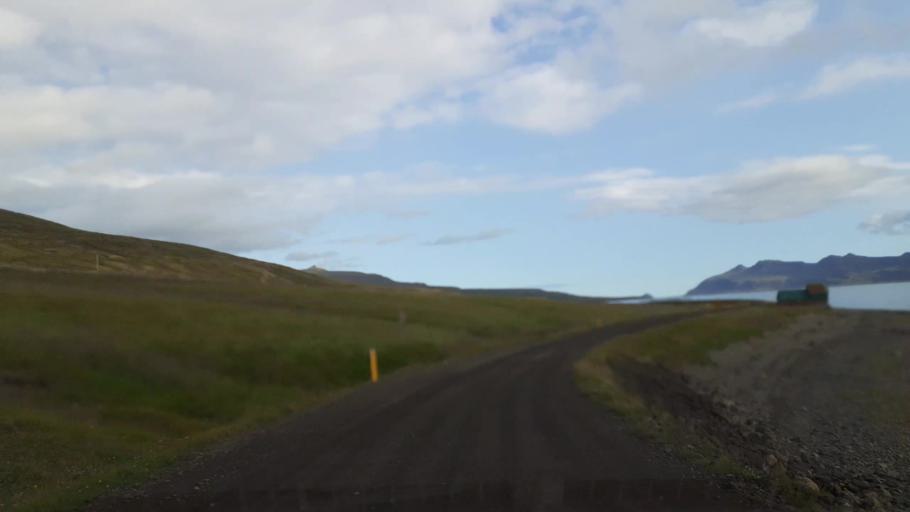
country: IS
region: East
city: Eskifjoerdur
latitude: 65.0374
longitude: -13.8767
